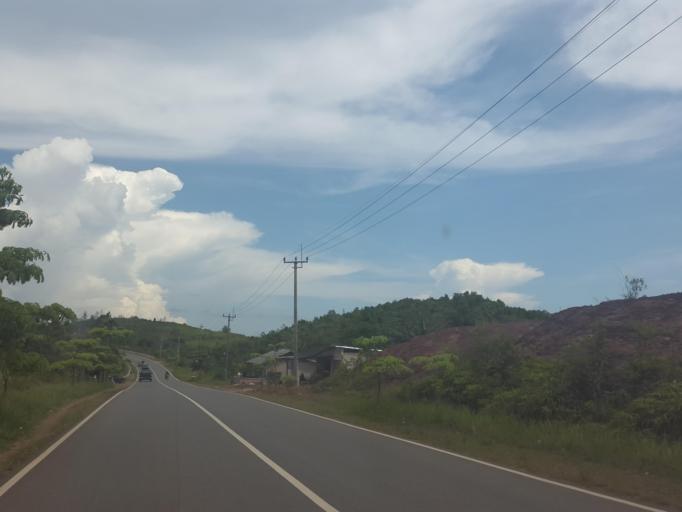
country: ID
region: Riau Islands
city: Tanjungpinang
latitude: 0.9098
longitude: 104.1229
